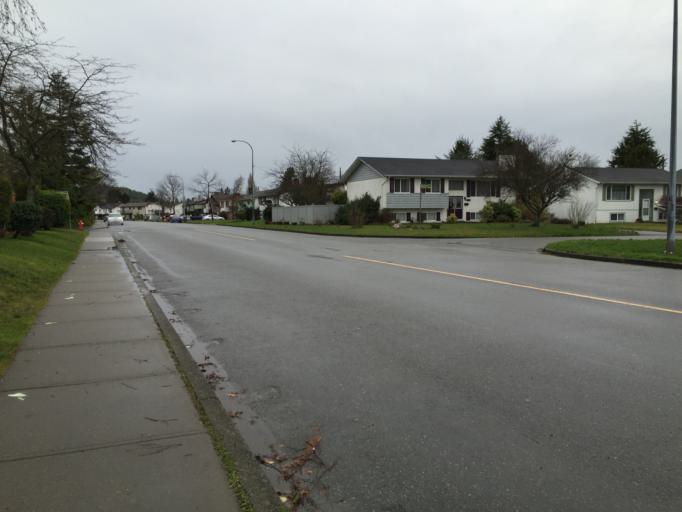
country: CA
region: British Columbia
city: Oak Bay
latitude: 48.4723
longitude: -123.3250
